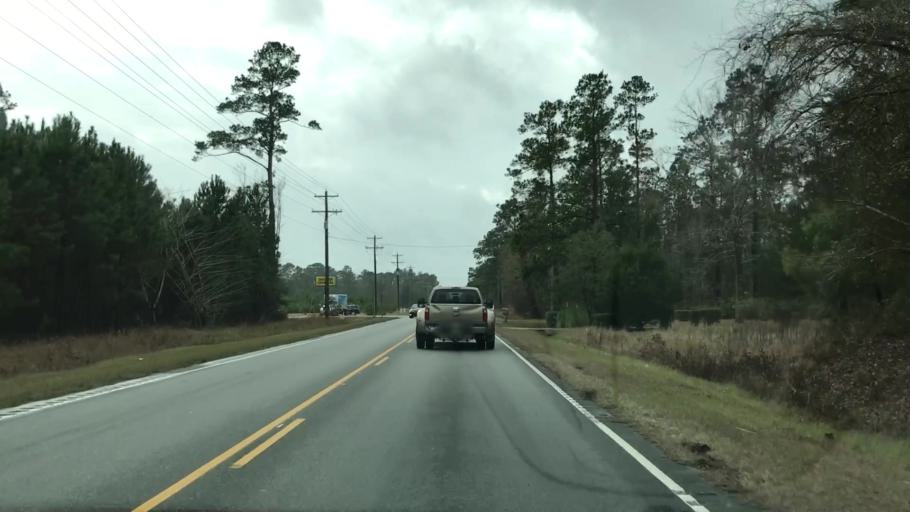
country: US
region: South Carolina
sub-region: Horry County
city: Socastee
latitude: 33.6967
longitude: -79.1124
